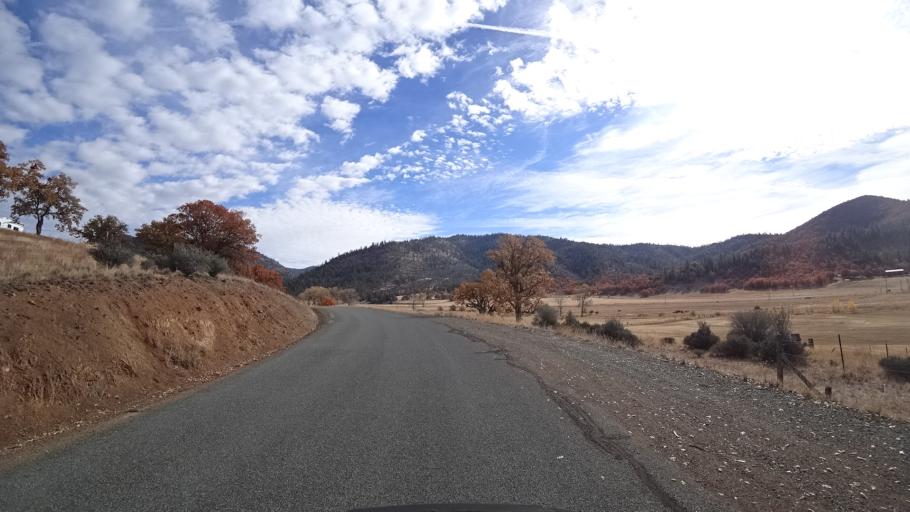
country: US
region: California
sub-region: Siskiyou County
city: Yreka
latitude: 41.6285
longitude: -122.7679
